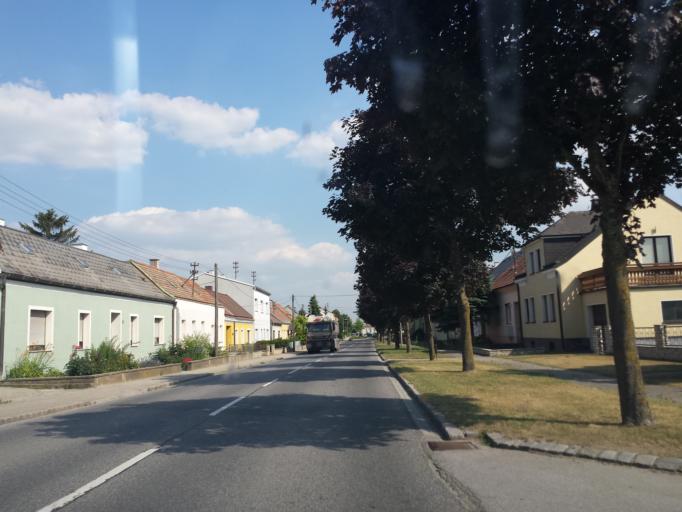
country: AT
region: Lower Austria
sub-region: Politischer Bezirk Ganserndorf
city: Markgrafneusiedl
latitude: 48.2699
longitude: 16.6280
